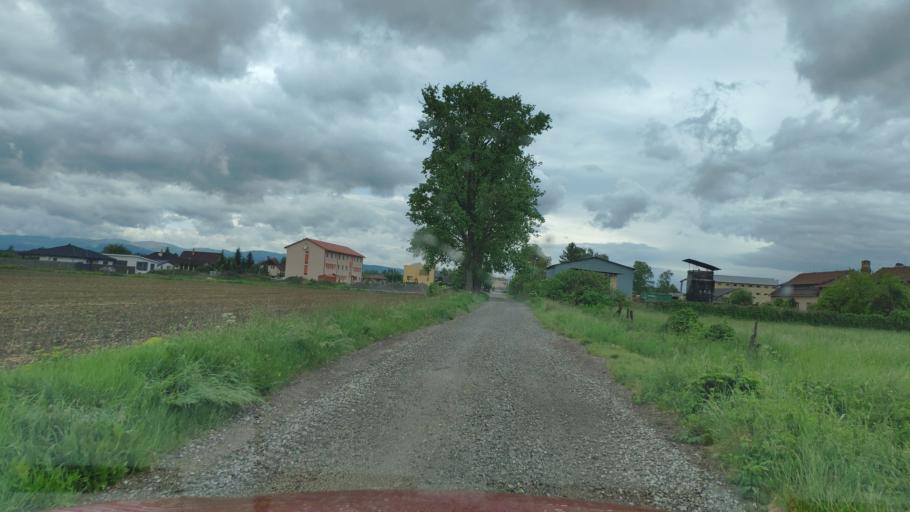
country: SK
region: Kosicky
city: Moldava nad Bodvou
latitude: 48.5685
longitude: 21.1215
